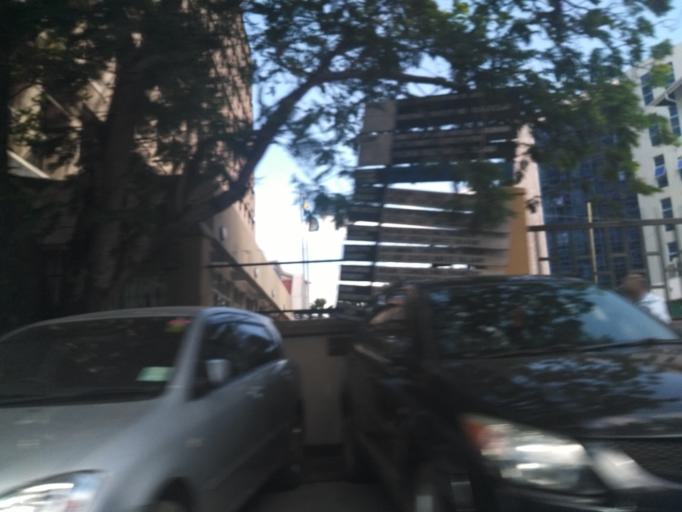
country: TZ
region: Dar es Salaam
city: Dar es Salaam
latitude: -6.8177
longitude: 39.2970
